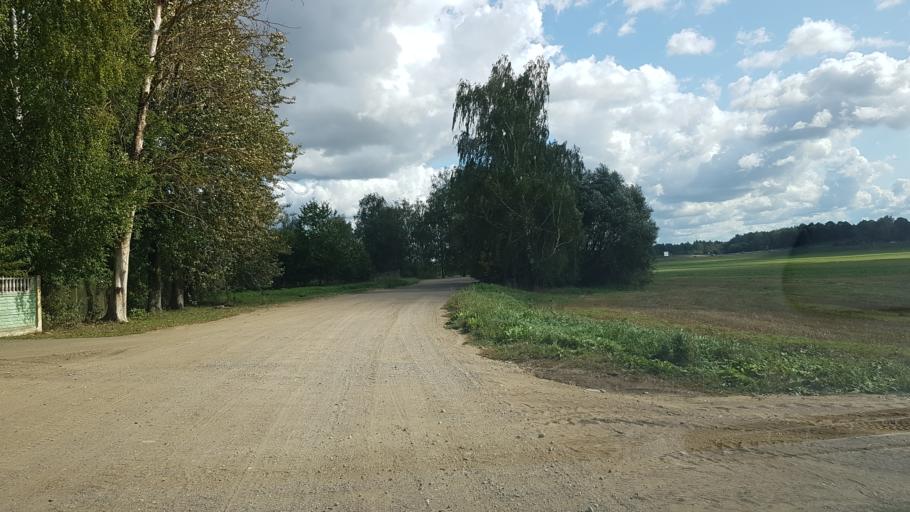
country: BY
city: Fanipol
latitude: 53.7378
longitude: 27.2914
